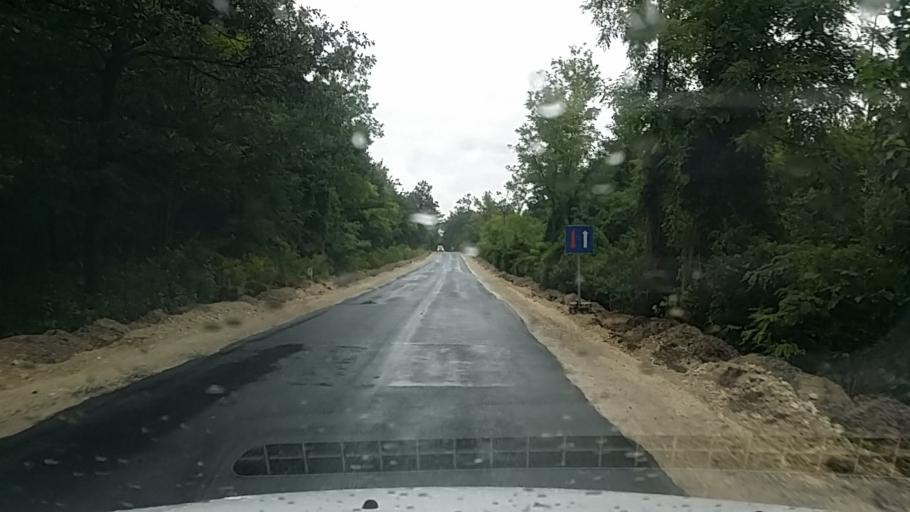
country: AT
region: Burgenland
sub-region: Eisenstadt-Umgebung
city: Morbisch am See
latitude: 47.7581
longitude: 16.6224
